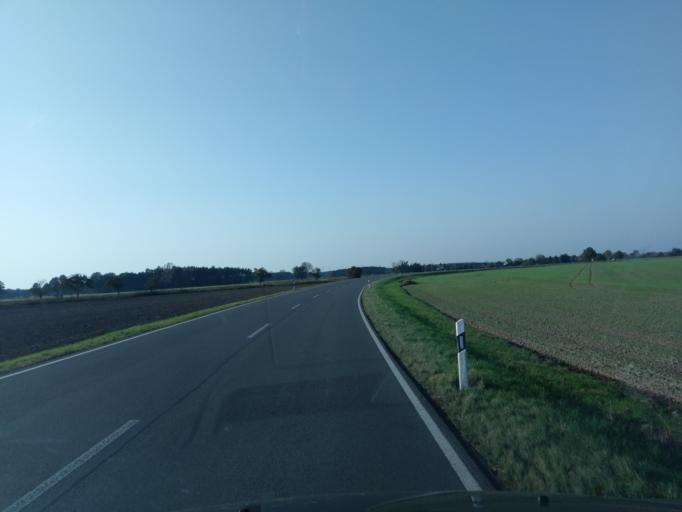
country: DE
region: Brandenburg
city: Falkenberg
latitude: 51.5323
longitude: 13.2937
